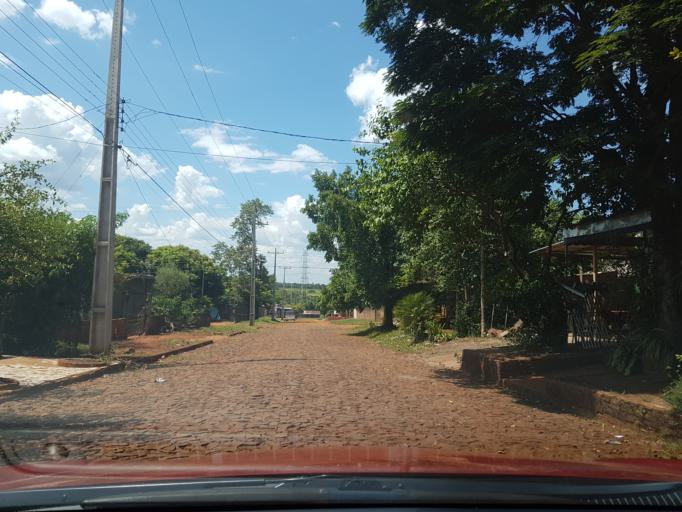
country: PY
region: Alto Parana
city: Ciudad del Este
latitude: -25.4810
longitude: -54.6811
